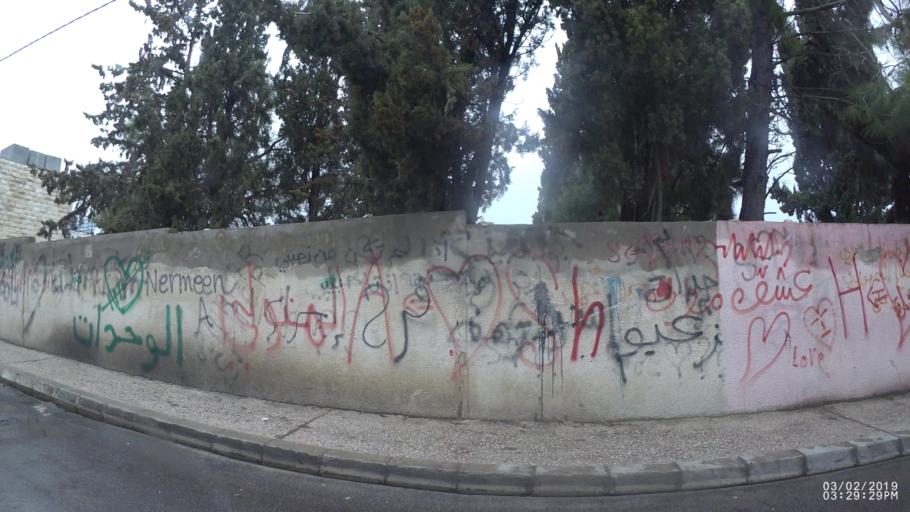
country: JO
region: Amman
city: Amman
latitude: 31.9613
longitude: 35.9289
